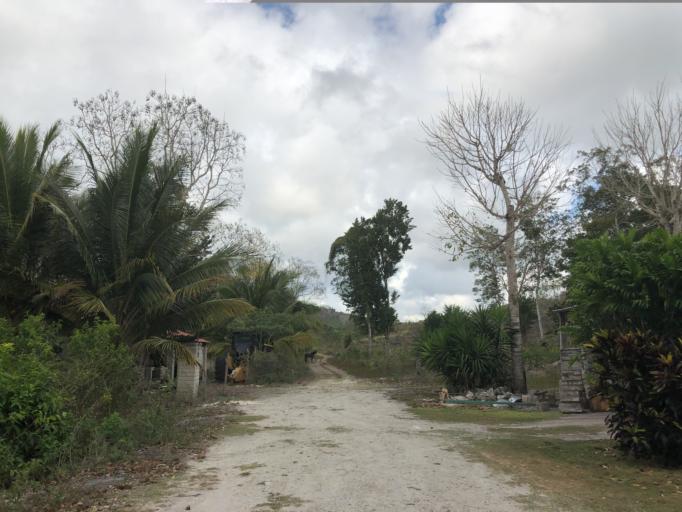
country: MX
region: Quintana Roo
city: Nicolas Bravo
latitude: 18.4516
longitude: -89.3088
